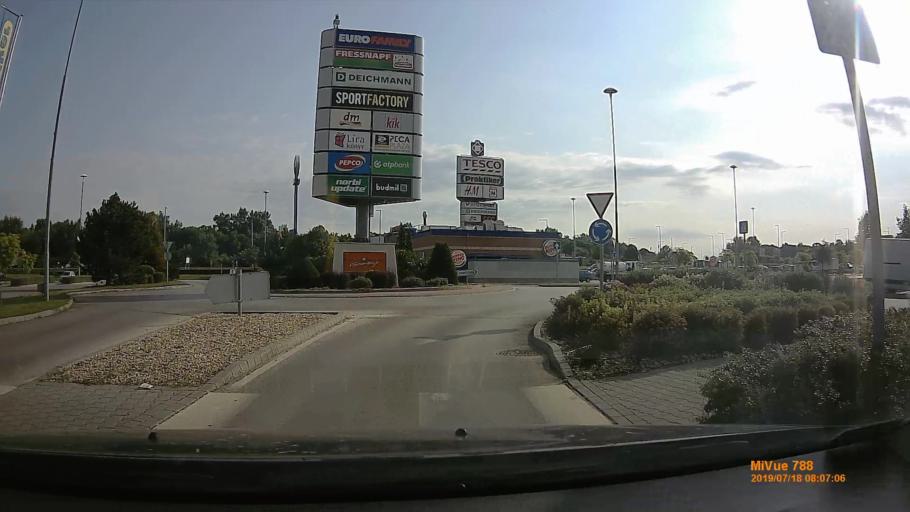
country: HU
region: Budapest
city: Budapest XIV. keruelet
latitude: 47.4934
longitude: 19.0975
